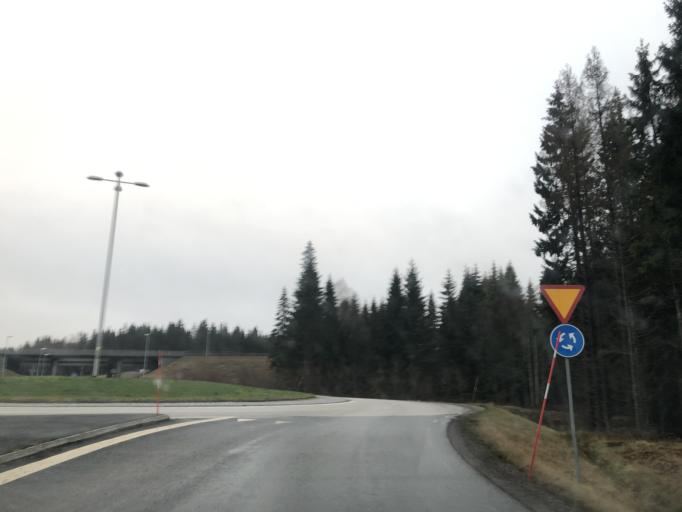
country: SE
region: Vaestra Goetaland
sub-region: Ulricehamns Kommun
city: Ulricehamn
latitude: 57.8209
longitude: 13.2854
